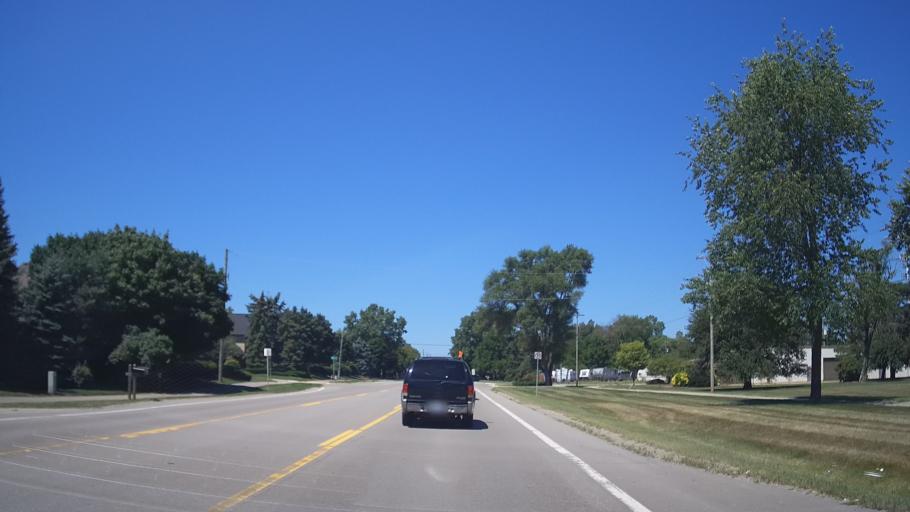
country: US
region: Michigan
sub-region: Oakland County
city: Rochester
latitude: 42.6532
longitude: -83.0984
